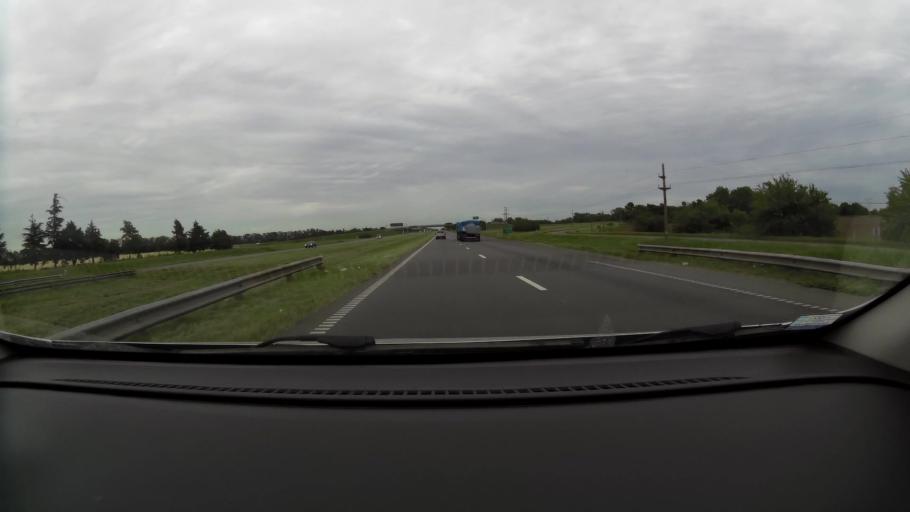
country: AR
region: Buenos Aires
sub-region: Partido de Zarate
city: Zarate
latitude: -34.0982
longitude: -59.1586
